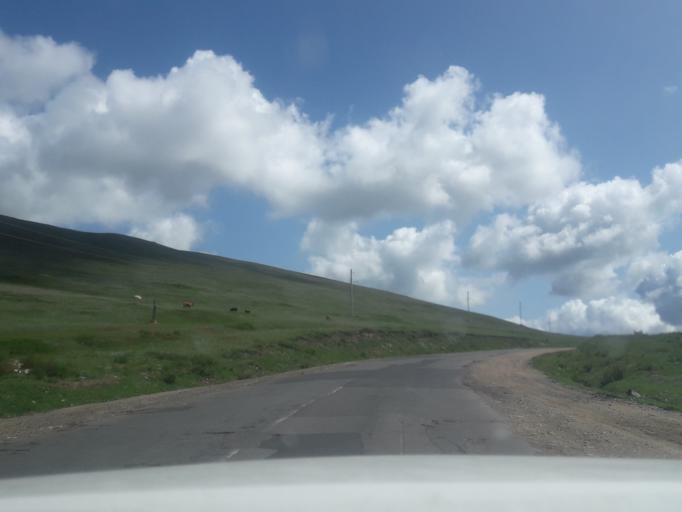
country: MN
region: Central Aimak
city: Ihsueuej
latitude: 48.1391
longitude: 106.4220
